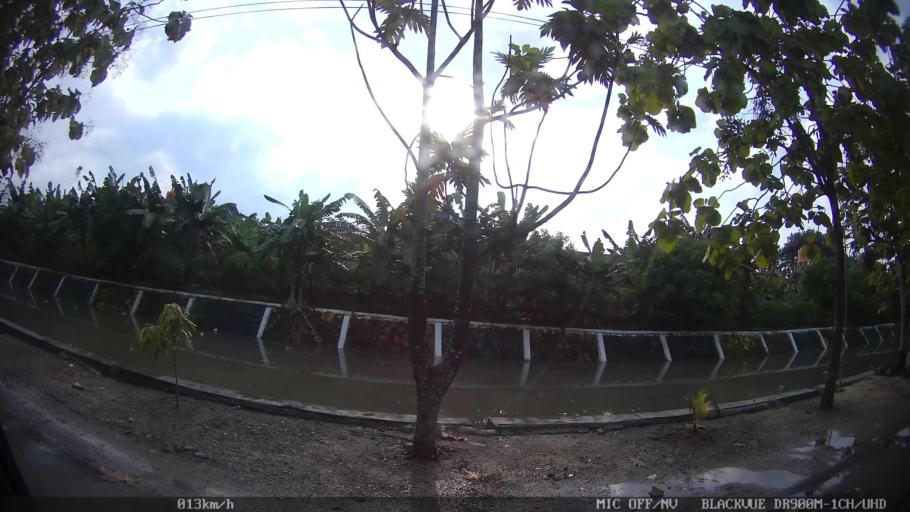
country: ID
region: Lampung
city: Kedaton
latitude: -5.3868
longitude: 105.3086
